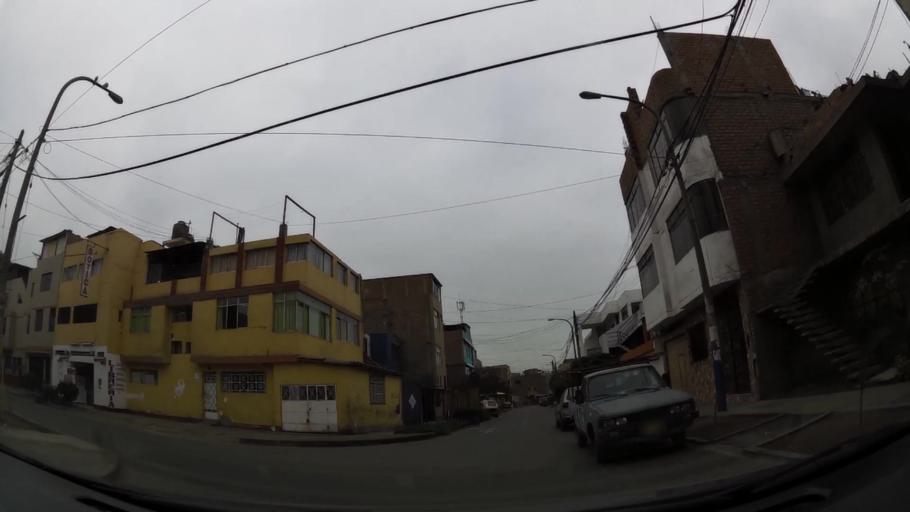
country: PE
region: Lima
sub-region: Lima
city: Independencia
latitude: -11.9714
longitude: -77.0584
